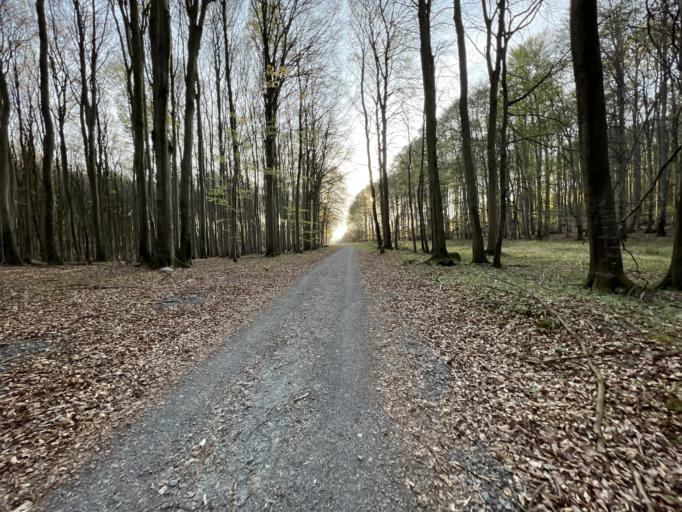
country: DE
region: Mecklenburg-Vorpommern
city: Sassnitz
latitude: 54.5360
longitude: 13.6613
